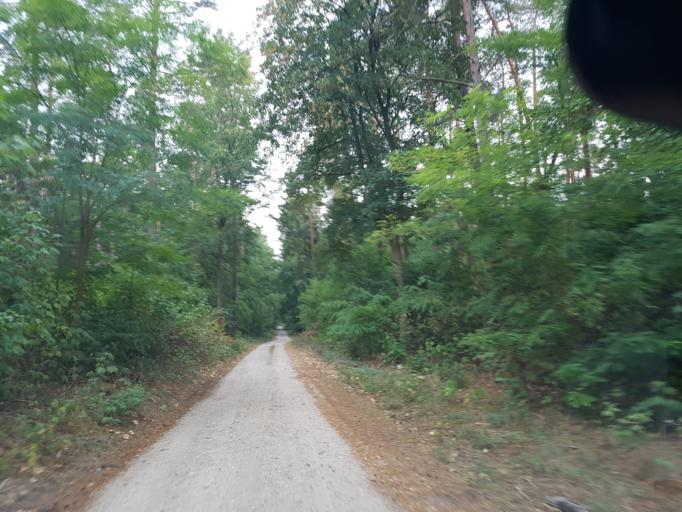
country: DE
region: Saxony-Anhalt
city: Rosslau
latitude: 52.0064
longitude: 12.2886
